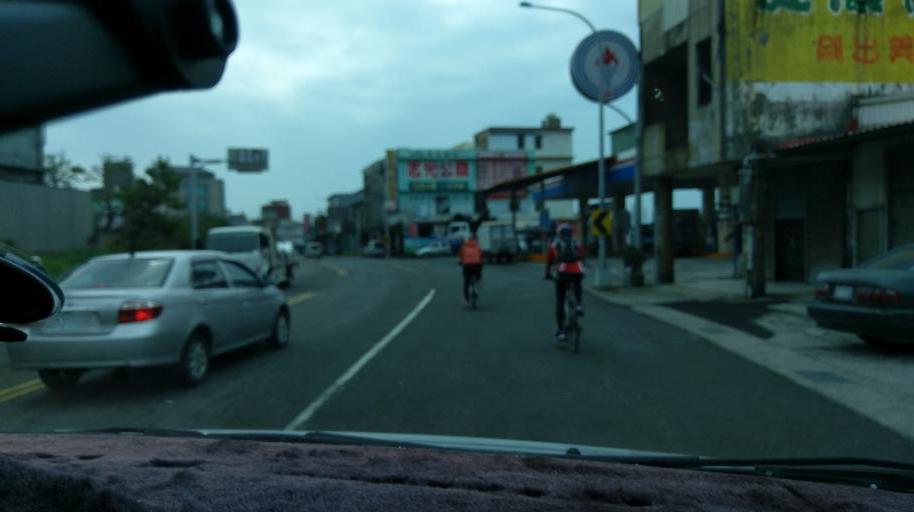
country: TW
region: Taiwan
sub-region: Miaoli
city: Miaoli
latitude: 24.4933
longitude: 120.6802
